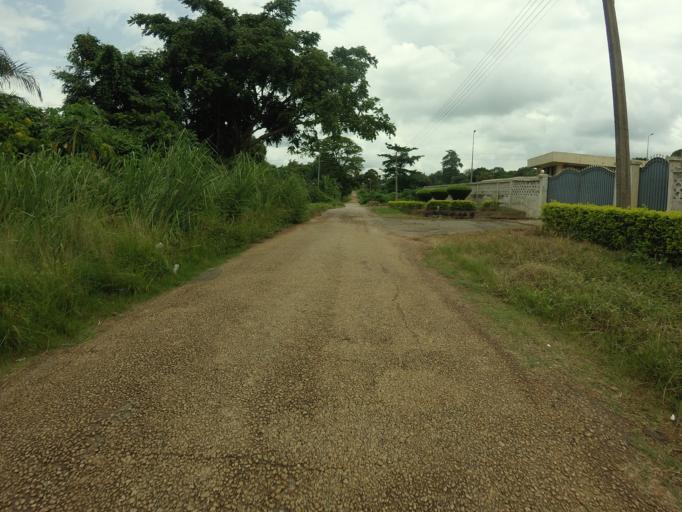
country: GH
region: Volta
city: Ho
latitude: 6.6043
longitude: 0.4625
